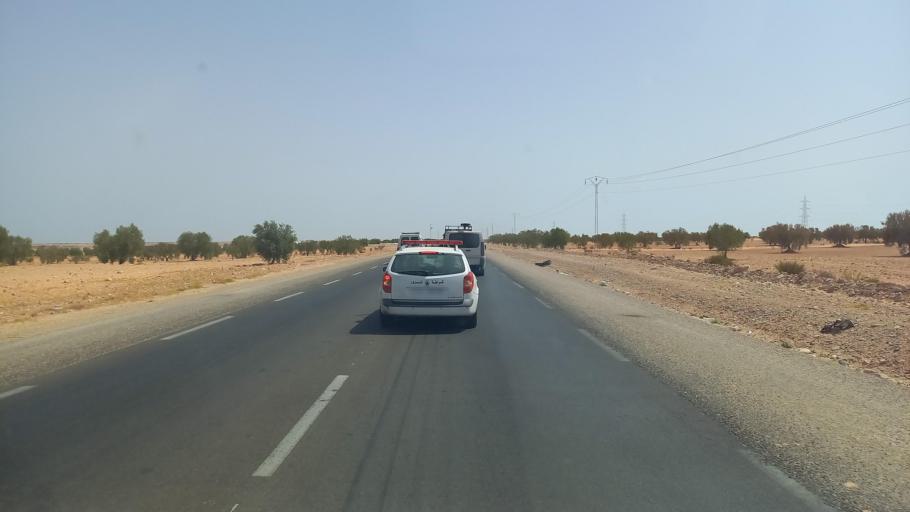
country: TN
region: Madanin
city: Zarzis
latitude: 33.3991
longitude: 10.8313
